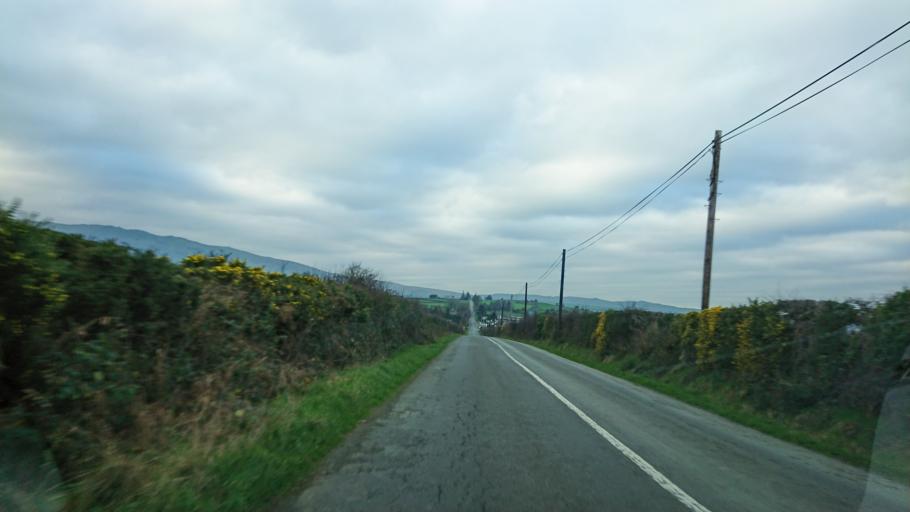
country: IE
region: Munster
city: Carrick-on-Suir
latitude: 52.3090
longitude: -7.5095
